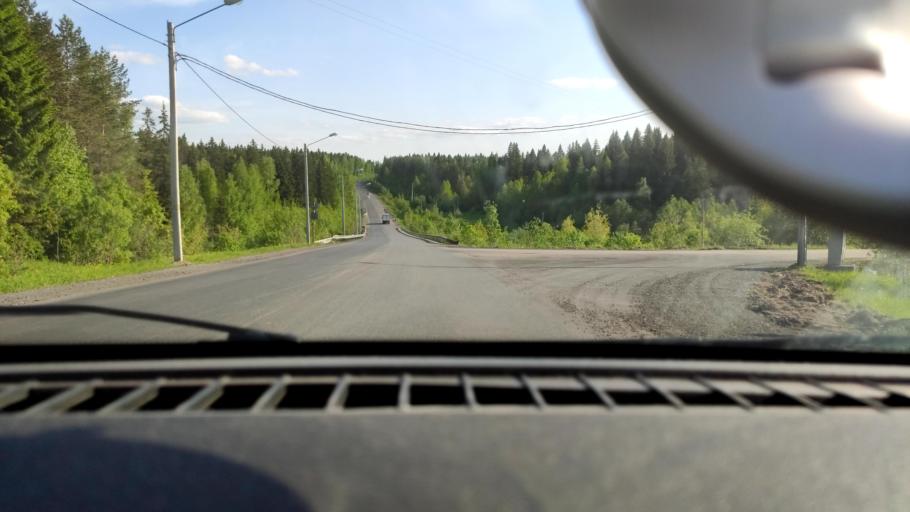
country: RU
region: Perm
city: Perm
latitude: 58.1427
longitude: 56.3038
